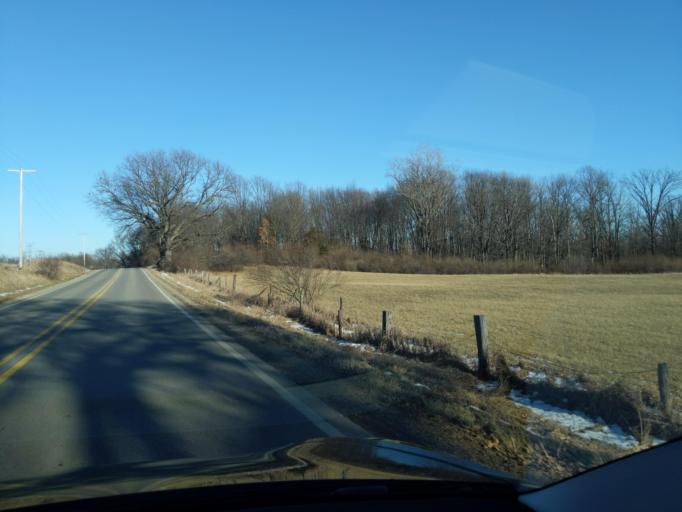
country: US
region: Michigan
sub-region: Ingham County
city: Stockbridge
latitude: 42.4162
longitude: -84.1822
